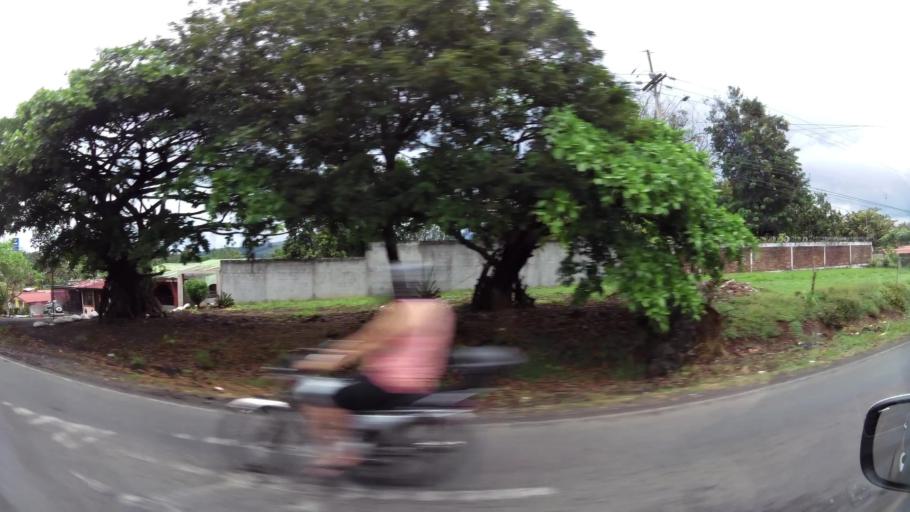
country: CR
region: Puntarenas
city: Esparza
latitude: 9.9954
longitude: -84.6720
